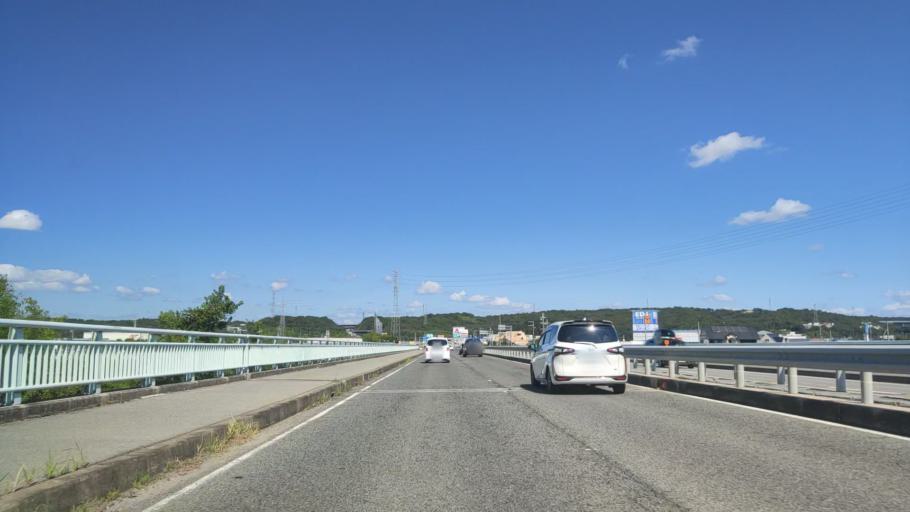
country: JP
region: Hyogo
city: Miki
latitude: 34.8002
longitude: 134.9663
